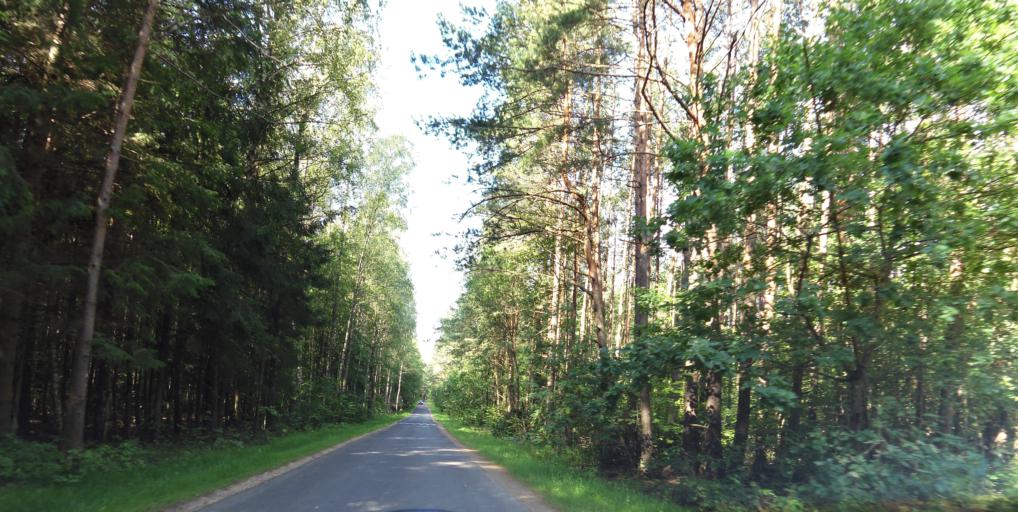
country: LT
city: Grigiskes
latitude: 54.7246
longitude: 25.0579
